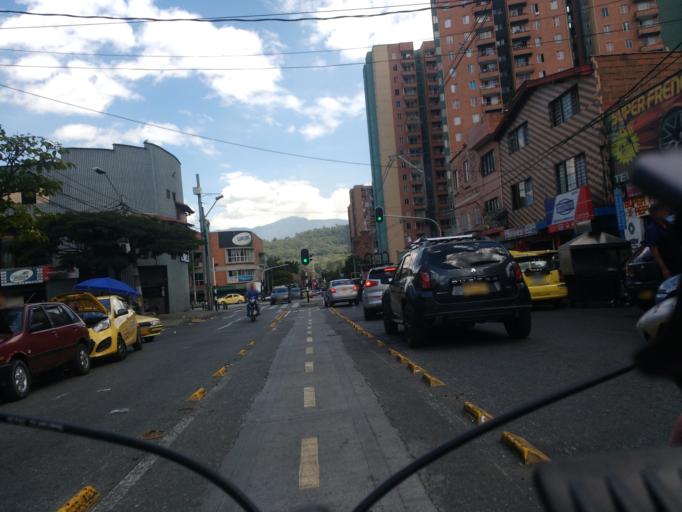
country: CO
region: Antioquia
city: Medellin
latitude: 6.2629
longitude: -75.5676
